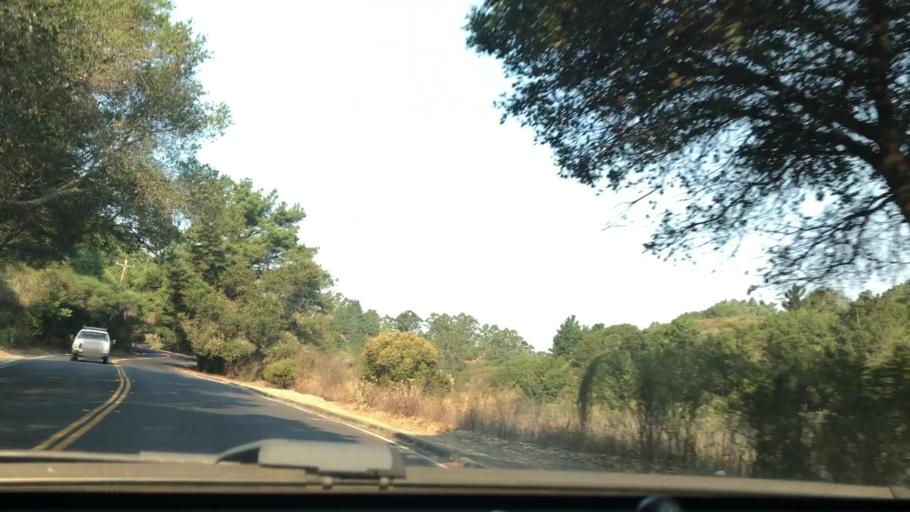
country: US
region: California
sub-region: Contra Costa County
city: Orinda
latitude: 37.8625
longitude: -122.2142
